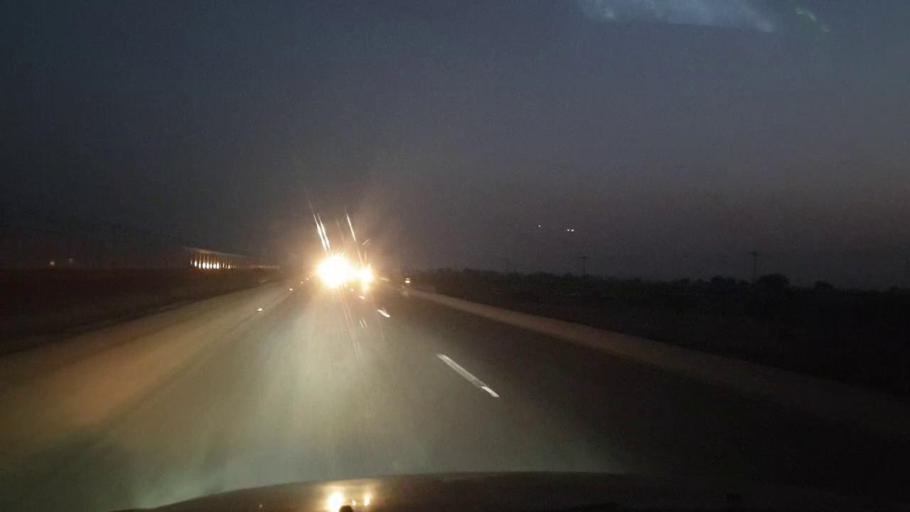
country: PK
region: Sindh
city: Chambar
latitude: 25.3431
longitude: 68.7933
